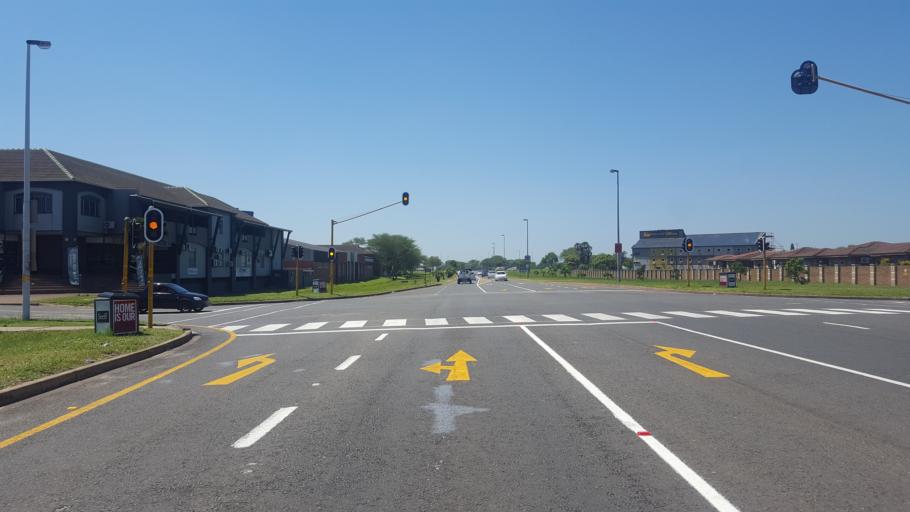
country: ZA
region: KwaZulu-Natal
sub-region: uThungulu District Municipality
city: Richards Bay
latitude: -28.7537
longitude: 32.0540
